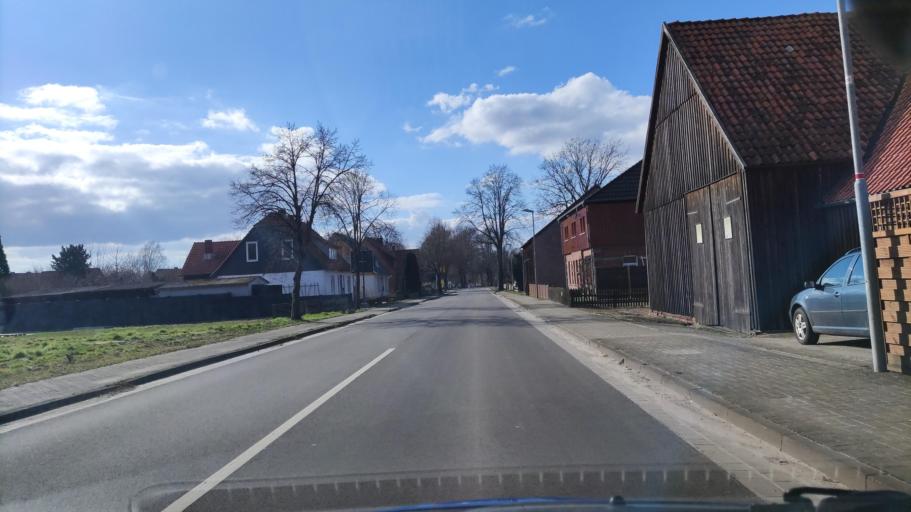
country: DE
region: Lower Saxony
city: Eldingen
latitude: 52.6859
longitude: 10.3391
